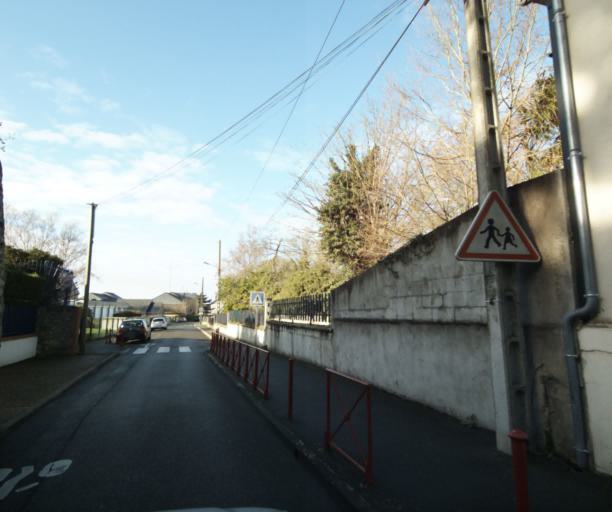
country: FR
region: Pays de la Loire
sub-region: Departement de la Sarthe
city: Coulaines
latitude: 48.0217
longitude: 0.2039
